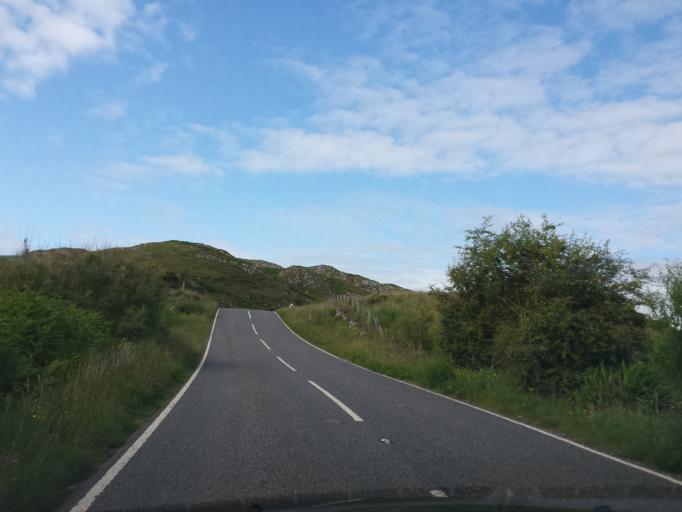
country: GB
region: Scotland
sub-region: Argyll and Bute
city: Isle Of Mull
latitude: 56.9581
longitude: -5.8417
